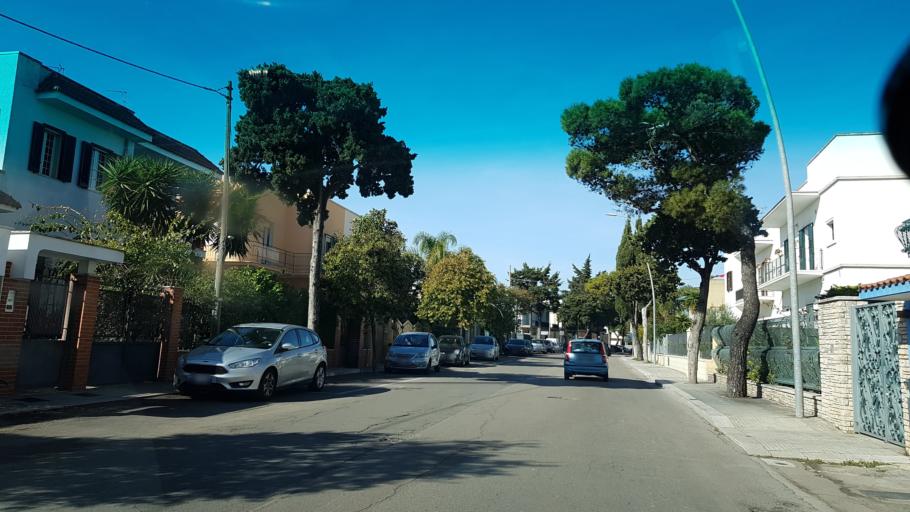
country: IT
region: Apulia
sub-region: Provincia di Lecce
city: Lecce
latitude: 40.3453
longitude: 18.1558
